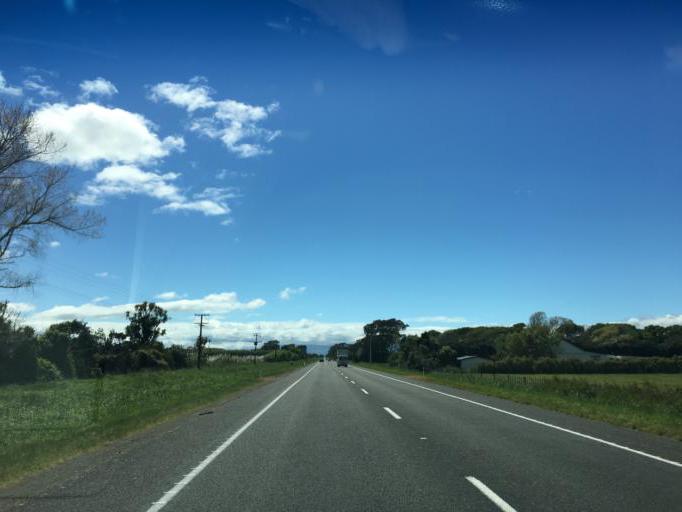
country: NZ
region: Manawatu-Wanganui
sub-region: Palmerston North City
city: Palmerston North
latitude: -40.3990
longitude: 175.5088
